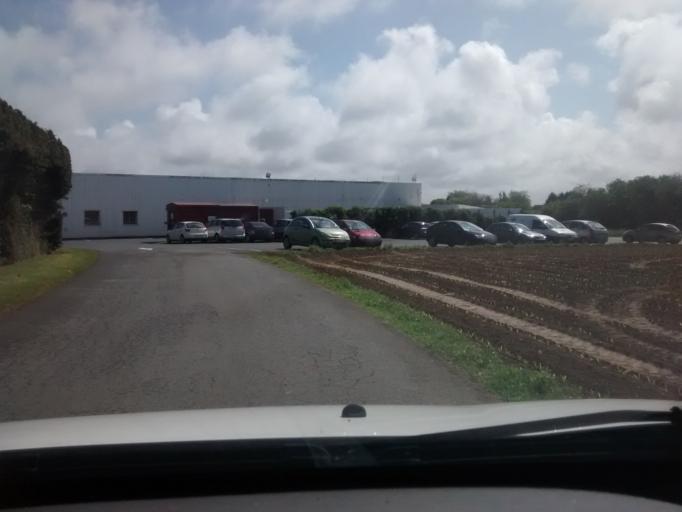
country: FR
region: Brittany
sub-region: Departement des Cotes-d'Armor
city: Penvenan
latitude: 48.8088
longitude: -3.2997
